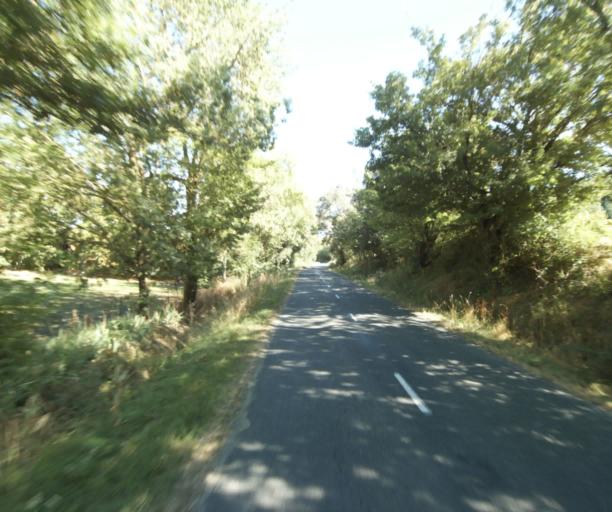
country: FR
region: Midi-Pyrenees
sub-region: Departement de la Haute-Garonne
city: Saint-Felix-Lauragais
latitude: 43.5174
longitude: 1.9302
